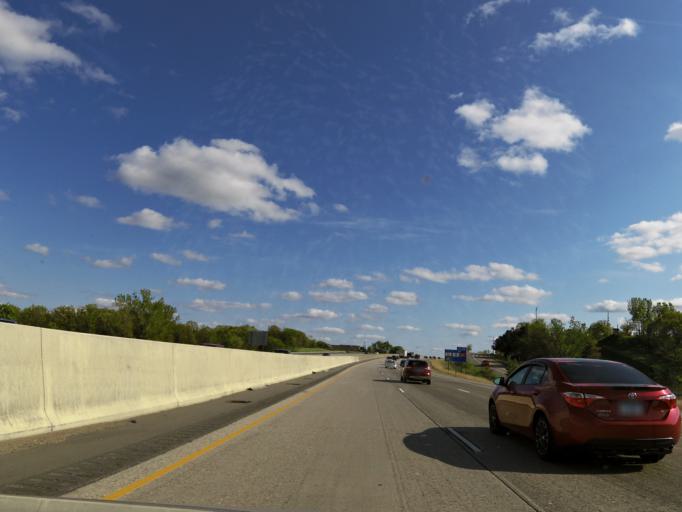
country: US
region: Minnesota
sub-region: Dakota County
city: Burnsville
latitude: 44.7238
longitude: -93.2819
